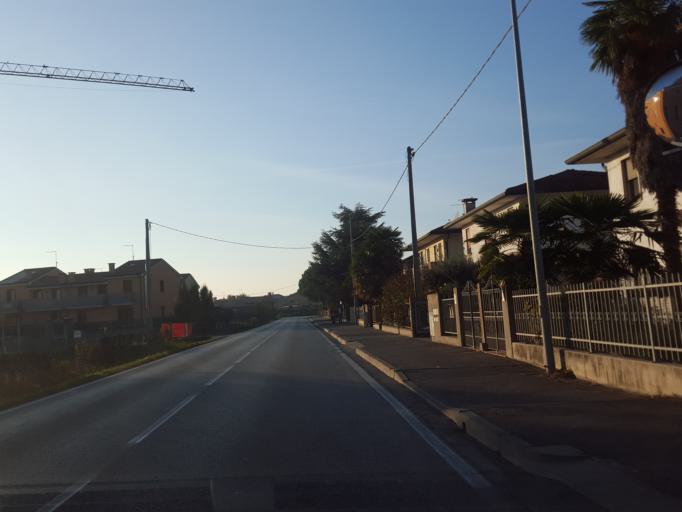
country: IT
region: Veneto
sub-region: Provincia di Vicenza
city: Camisano Vicentino
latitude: 45.5210
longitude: 11.7224
